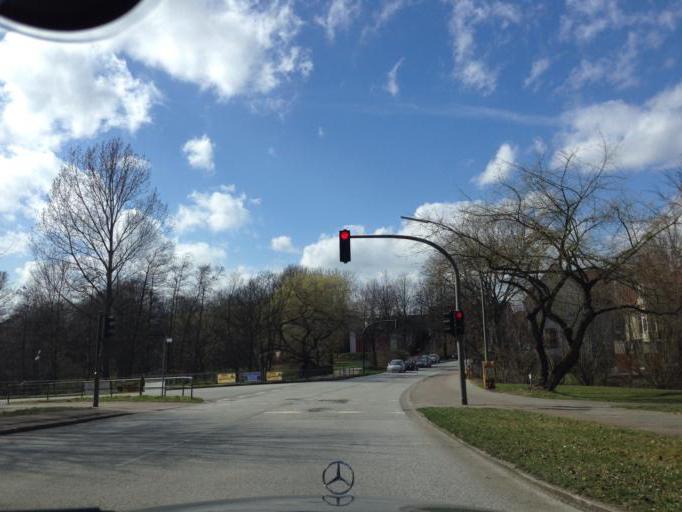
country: DE
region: Hamburg
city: Wandsbek
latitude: 53.5379
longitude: 10.1158
